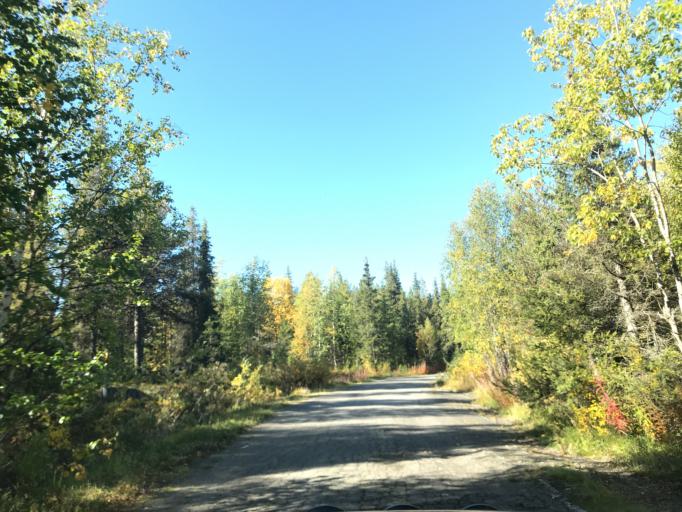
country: SE
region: Norrbotten
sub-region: Gallivare Kommun
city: Malmberget
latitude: 67.6463
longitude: 21.0741
